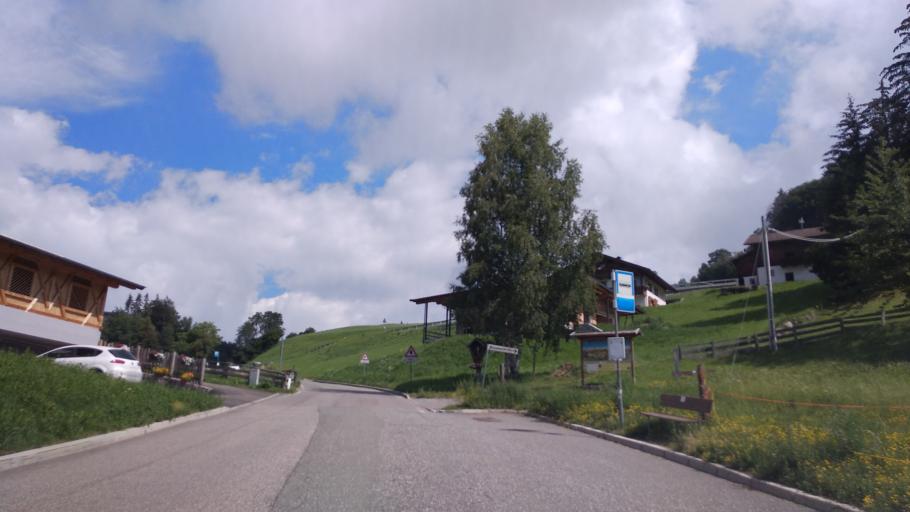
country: IT
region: Trentino-Alto Adige
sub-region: Bolzano
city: Avelengo
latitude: 46.6492
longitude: 11.2178
